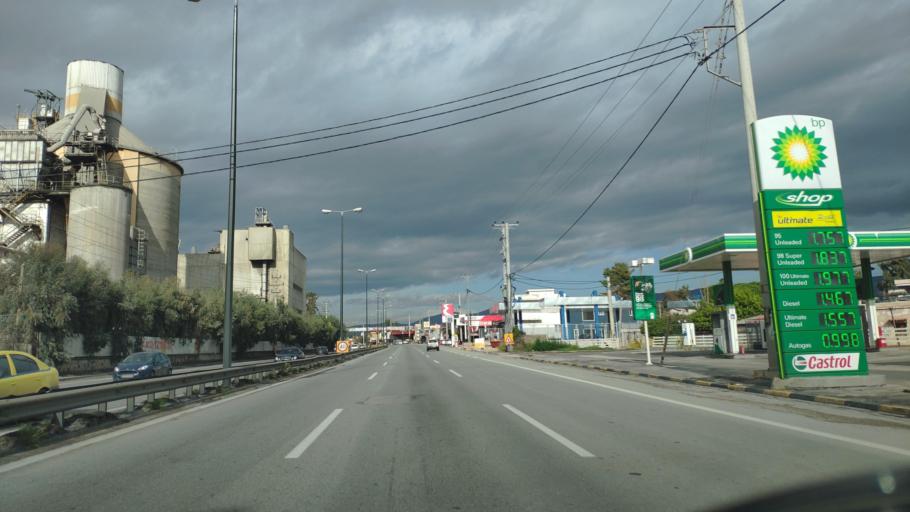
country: GR
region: Attica
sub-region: Nomarchia Dytikis Attikis
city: Aspropyrgos
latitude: 38.0346
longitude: 23.5945
